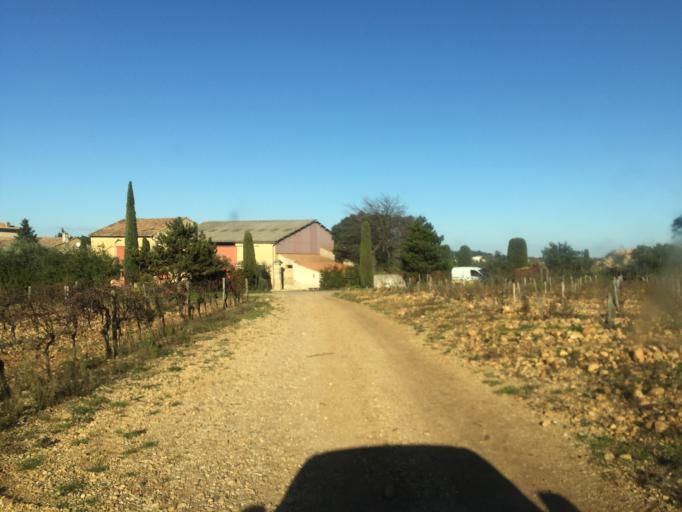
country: FR
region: Provence-Alpes-Cote d'Azur
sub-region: Departement du Vaucluse
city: Bedarrides
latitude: 44.0303
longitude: 4.8890
